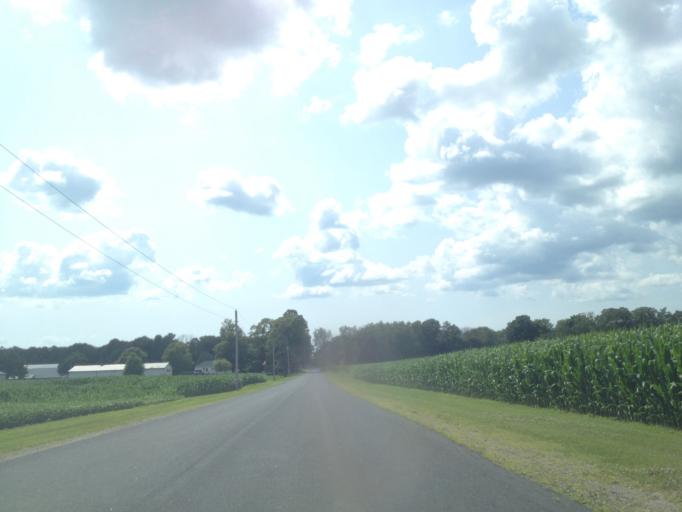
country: CA
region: Ontario
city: Aylmer
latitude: 42.6810
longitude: -80.9929
